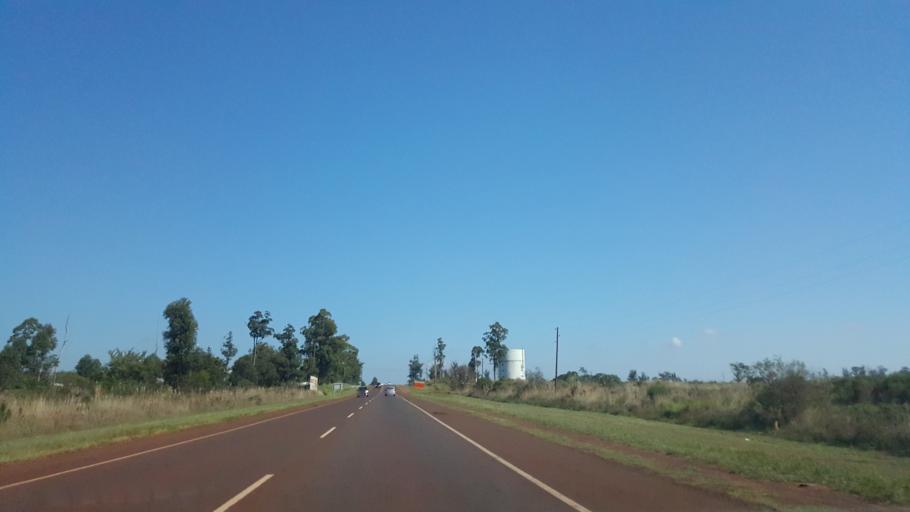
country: AR
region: Misiones
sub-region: Departamento de Capital
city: Posadas
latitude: -27.4184
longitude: -55.9898
